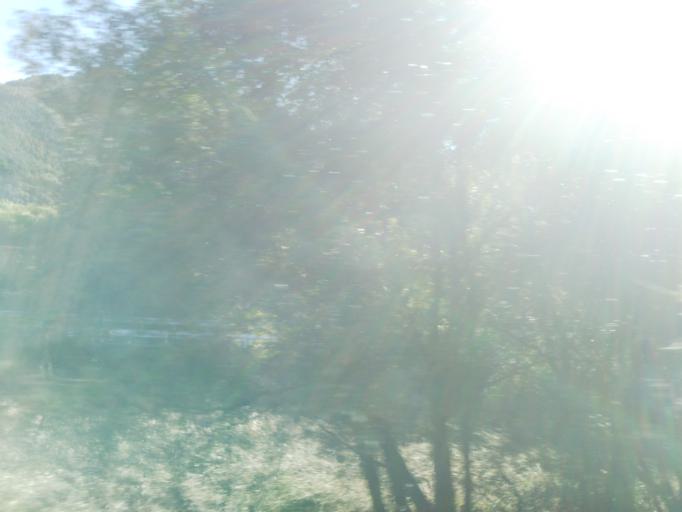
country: JP
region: Kochi
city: Nakamura
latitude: 33.1106
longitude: 133.1071
